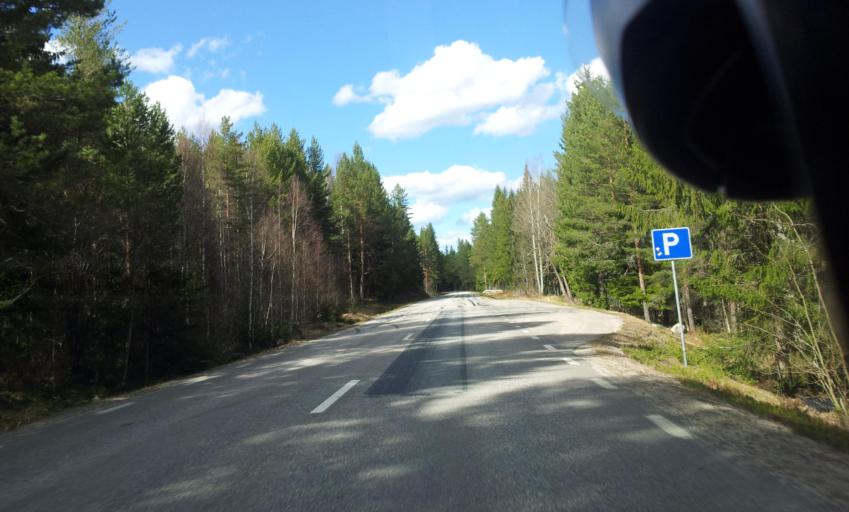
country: SE
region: Gaevleborg
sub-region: Ovanakers Kommun
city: Edsbyn
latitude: 61.3517
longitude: 15.8146
